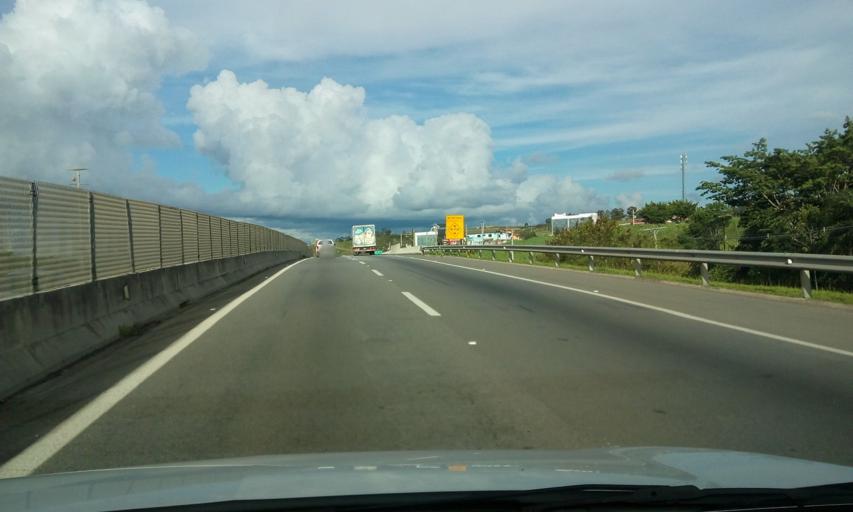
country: BR
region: Sao Paulo
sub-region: Jundiai
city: Jundiai
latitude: -23.1619
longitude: -46.9050
